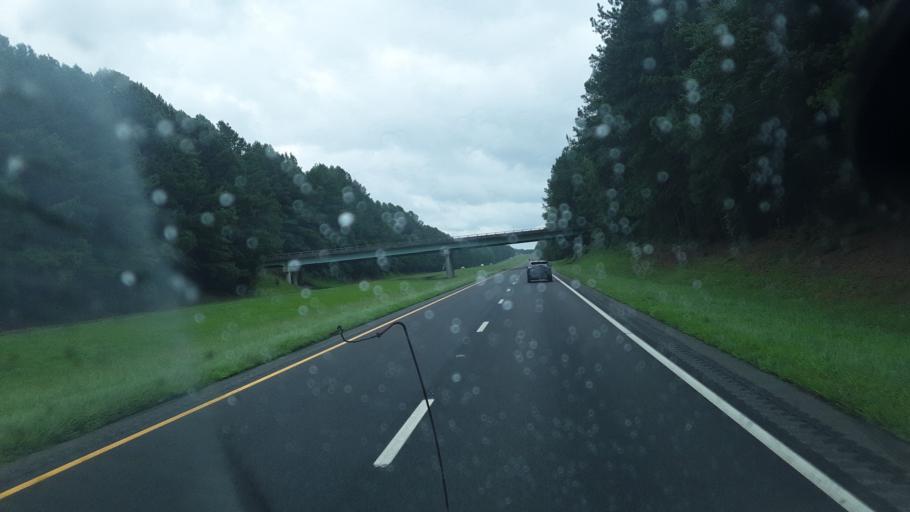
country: US
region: North Carolina
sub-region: Montgomery County
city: Biscoe
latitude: 35.3346
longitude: -79.7510
